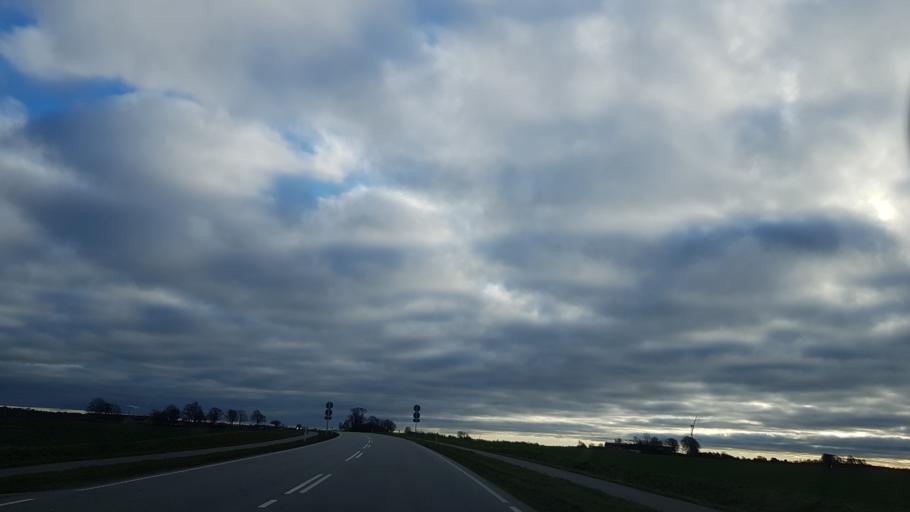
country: DK
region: Zealand
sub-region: Kalundborg Kommune
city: Gorlev
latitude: 55.5178
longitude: 11.2442
